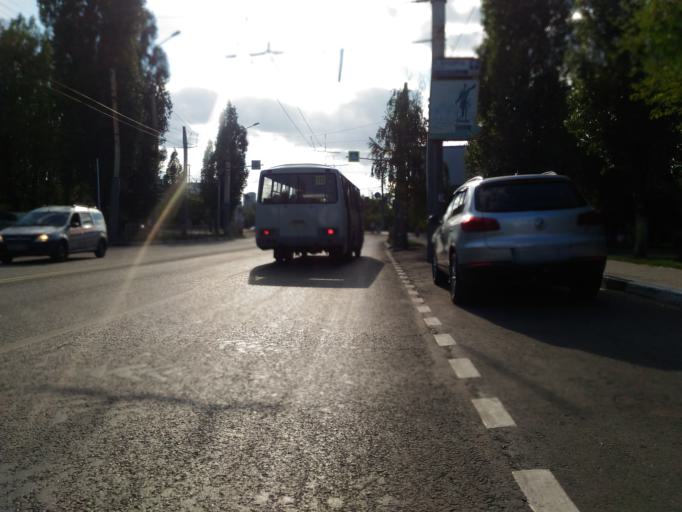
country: RU
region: Voronezj
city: Voronezh
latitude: 51.6519
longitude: 39.1385
